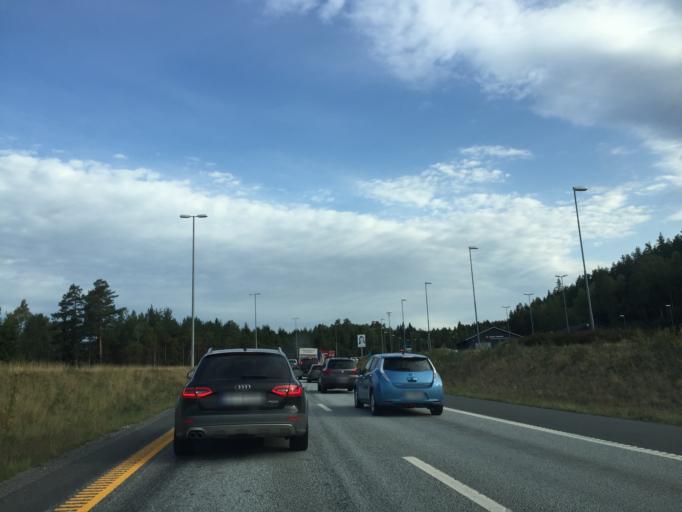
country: NO
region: Akershus
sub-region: Oppegard
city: Kolbotn
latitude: 59.8107
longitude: 10.8401
